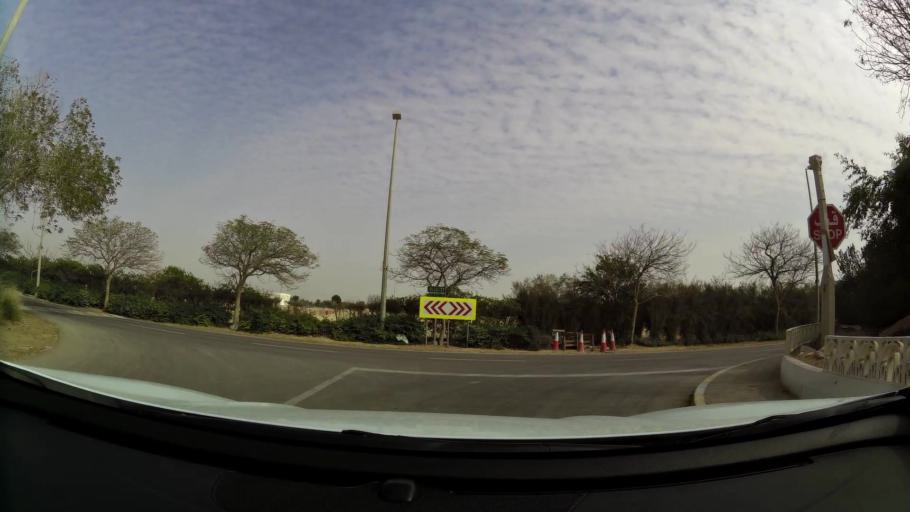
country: AE
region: Abu Dhabi
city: Abu Dhabi
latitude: 24.6043
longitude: 54.7056
